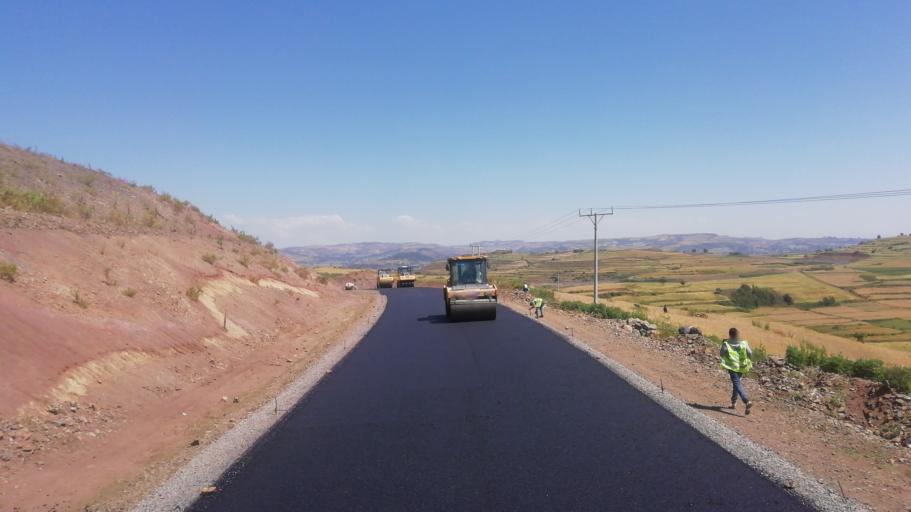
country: ET
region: Amhara
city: Addiet Canna
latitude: 11.3679
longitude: 37.8718
